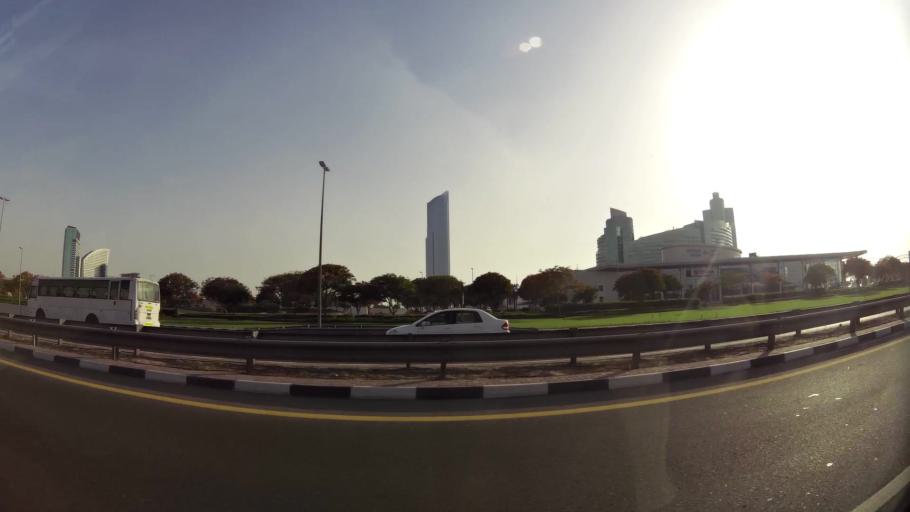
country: AE
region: Ash Shariqah
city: Sharjah
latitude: 25.2323
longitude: 55.3514
